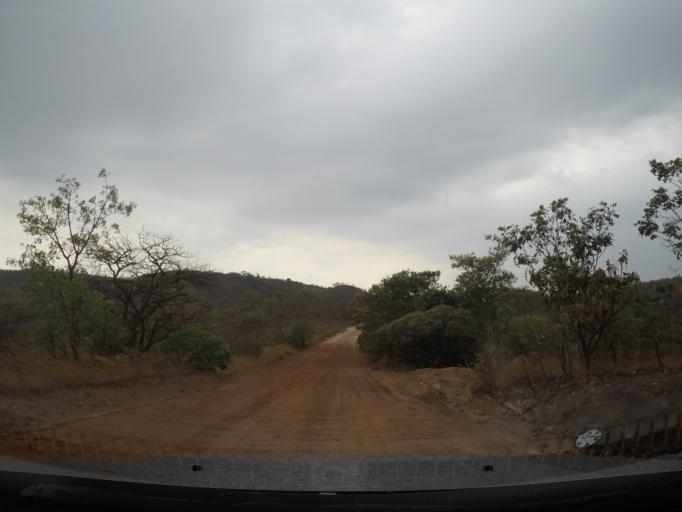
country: BR
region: Goias
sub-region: Pirenopolis
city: Pirenopolis
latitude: -15.8184
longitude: -48.8995
